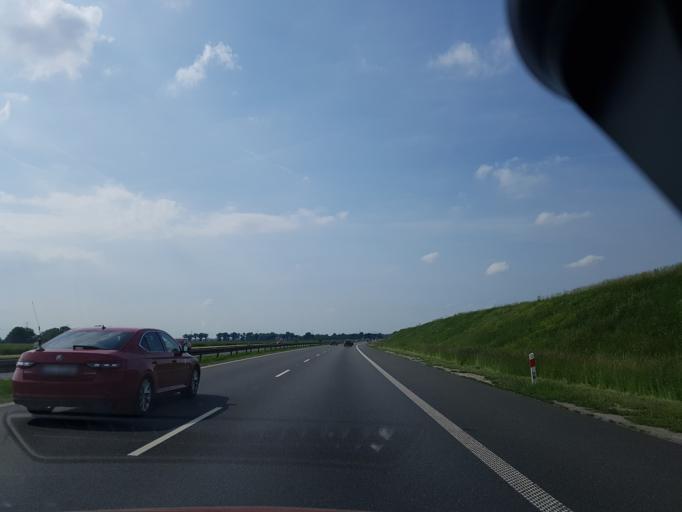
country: PL
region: Lower Silesian Voivodeship
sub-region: Powiat wroclawski
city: Zorawina
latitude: 50.9463
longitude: 17.0913
